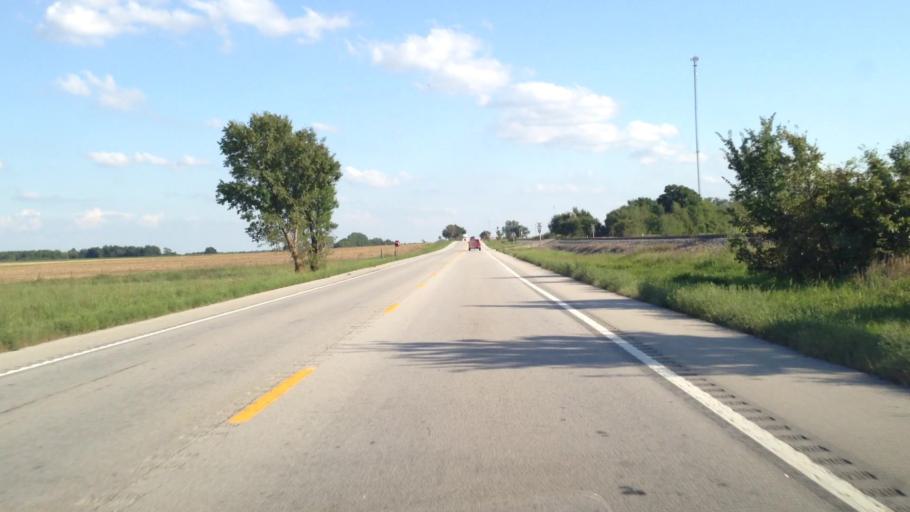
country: US
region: Missouri
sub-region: Jasper County
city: Carl Junction
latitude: 37.2656
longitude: -94.5963
